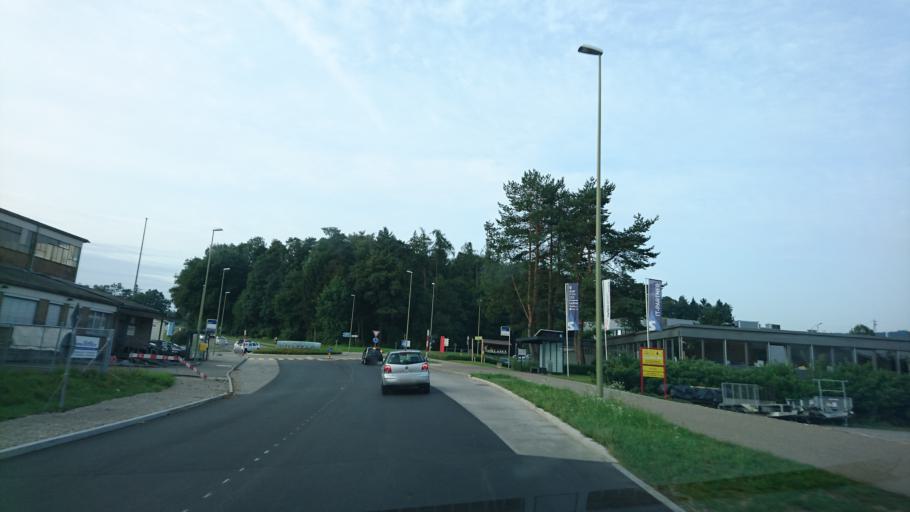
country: CH
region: Zurich
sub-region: Bezirk Uster
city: Moenchaltorf / Dorf
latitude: 47.3022
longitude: 8.7200
